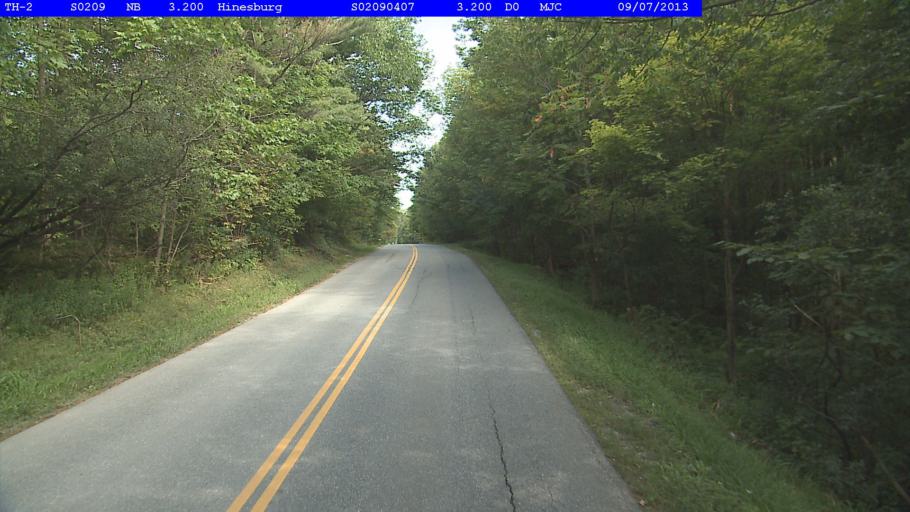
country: US
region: Vermont
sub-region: Chittenden County
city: Hinesburg
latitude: 44.3571
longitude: -73.0745
